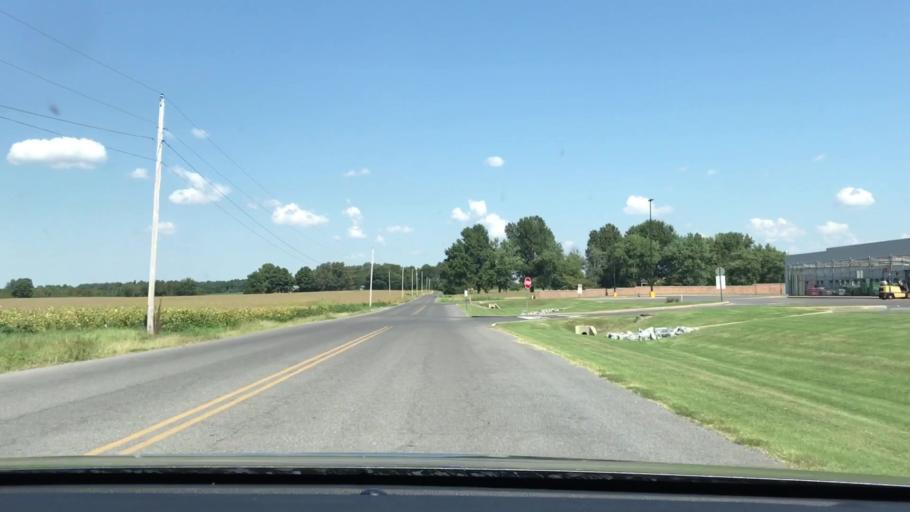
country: US
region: Kentucky
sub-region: Fulton County
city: Fulton
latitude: 36.5165
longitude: -88.9014
